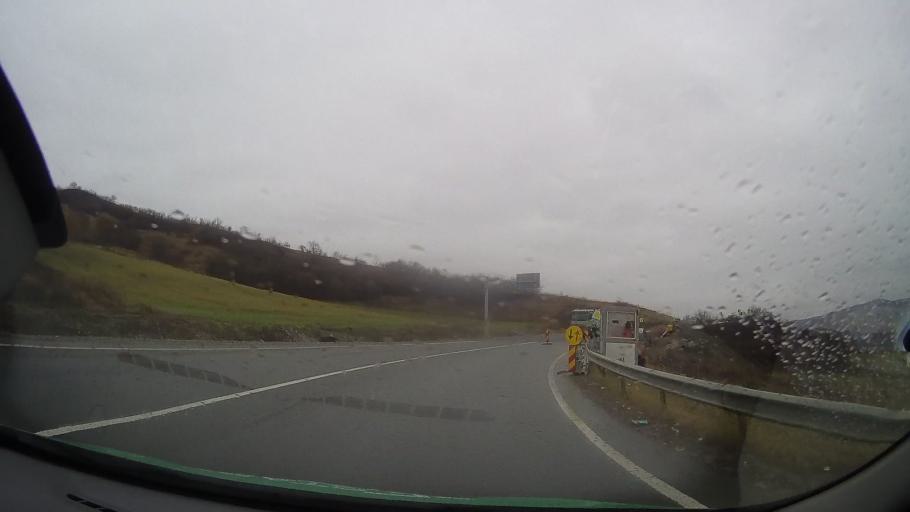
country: RO
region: Bistrita-Nasaud
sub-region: Comuna Teaca
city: Teaca
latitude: 46.9043
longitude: 24.4994
